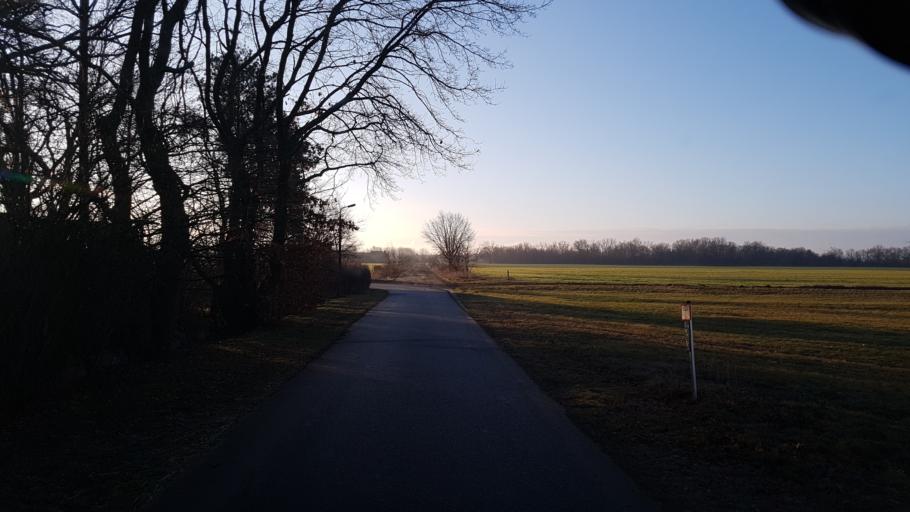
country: DE
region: Brandenburg
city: Falkenberg
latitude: 51.5618
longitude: 13.2232
